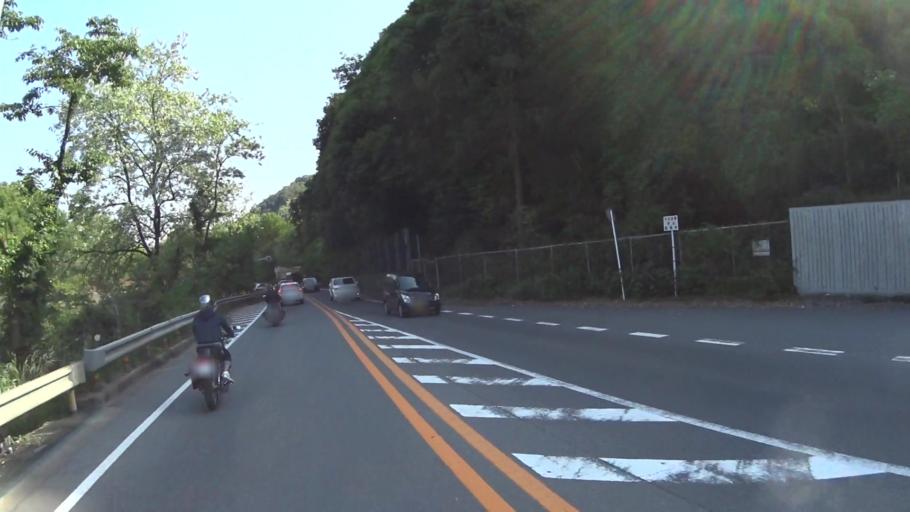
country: JP
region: Kyoto
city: Muko
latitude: 34.9857
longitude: 135.6535
